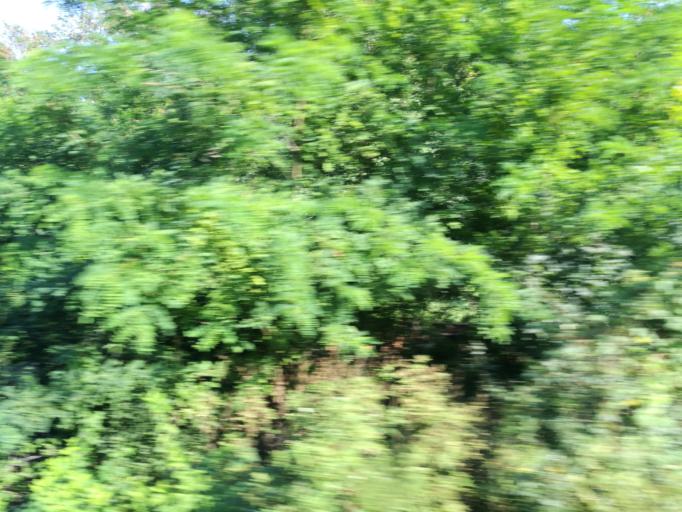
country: RO
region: Iasi
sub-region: Comuna Ciurea
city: Ciurea
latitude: 47.0178
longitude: 27.5777
